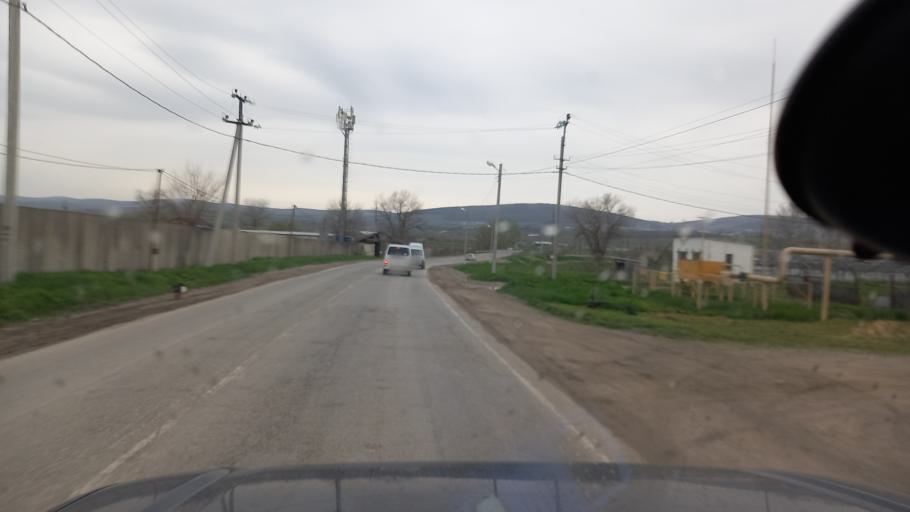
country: RU
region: Krasnodarskiy
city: Anapskaya
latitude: 44.8917
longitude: 37.4598
